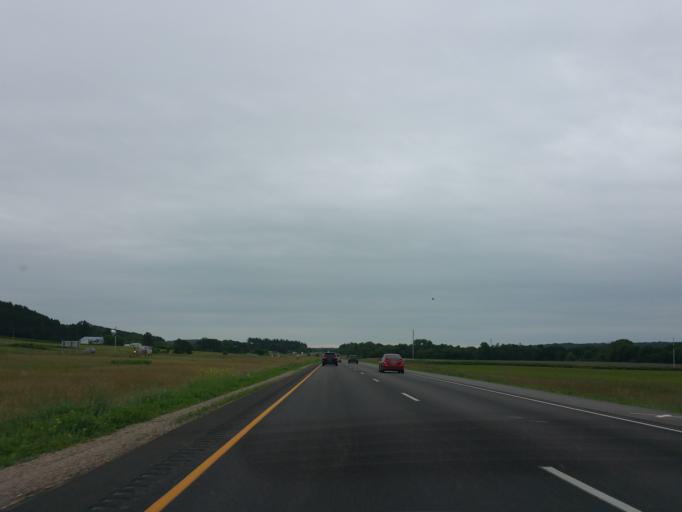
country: US
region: Wisconsin
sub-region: Eau Claire County
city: Altoona
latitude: 44.7441
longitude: -91.3795
